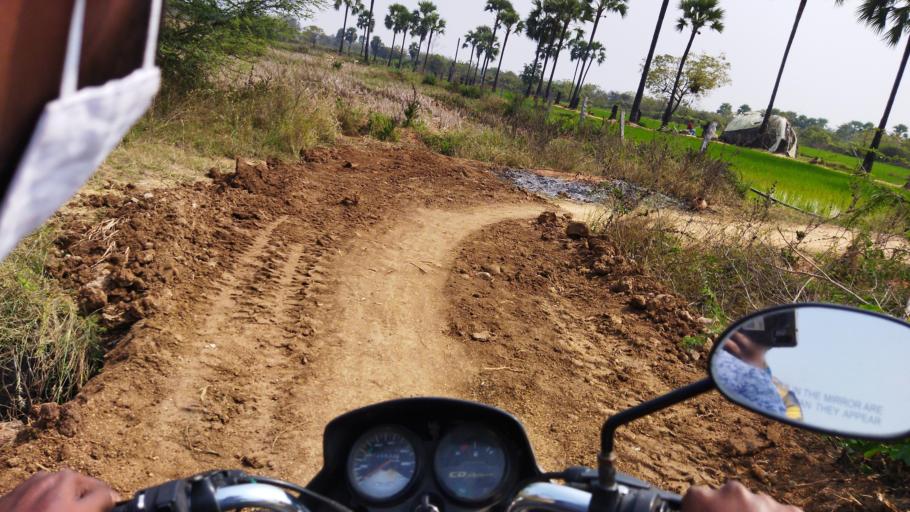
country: IN
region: Telangana
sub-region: Nalgonda
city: Nalgonda
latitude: 17.1515
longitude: 79.4093
